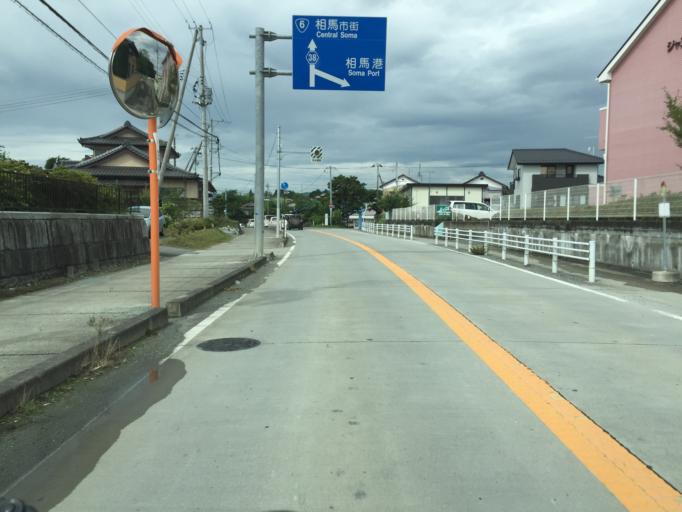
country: JP
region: Miyagi
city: Marumori
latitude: 37.8232
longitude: 140.9495
